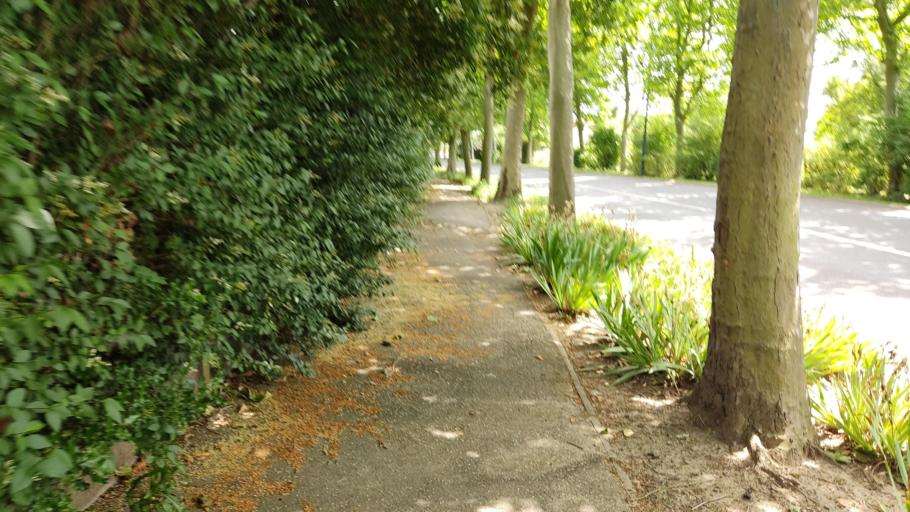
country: FR
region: Nord-Pas-de-Calais
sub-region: Departement du Pas-de-Calais
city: Henin-Beaumont
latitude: 50.4128
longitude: 2.9532
